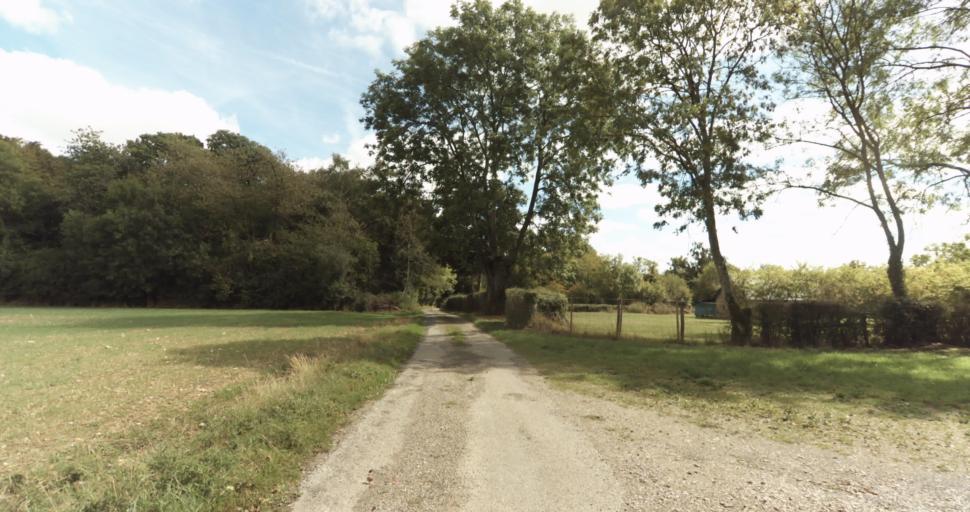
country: FR
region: Lower Normandy
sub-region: Departement du Calvados
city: Orbec
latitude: 48.9181
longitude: 0.3511
